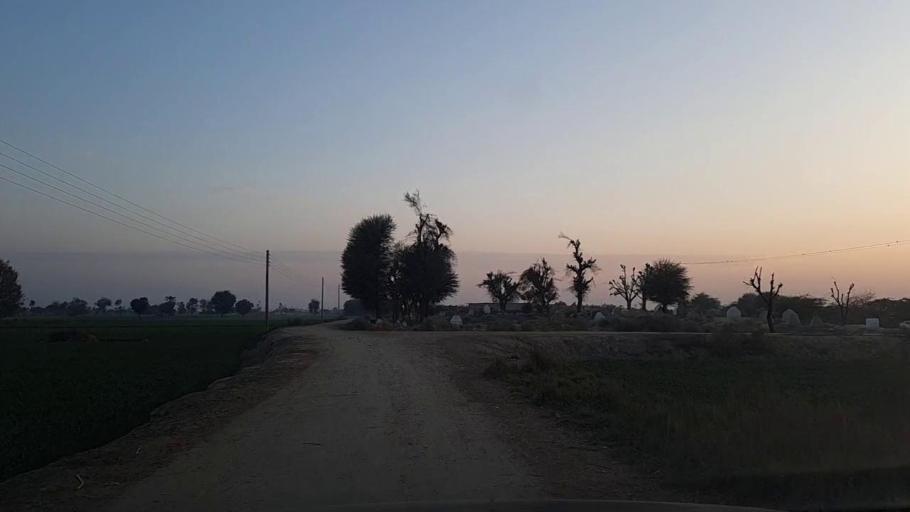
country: PK
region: Sindh
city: Jam Sahib
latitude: 26.4606
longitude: 68.5215
